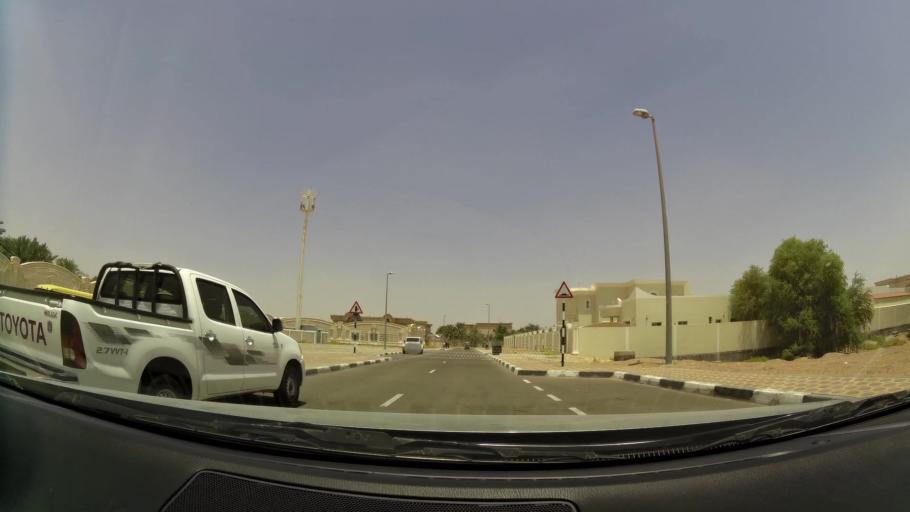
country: OM
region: Al Buraimi
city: Al Buraymi
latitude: 24.2690
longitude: 55.7154
